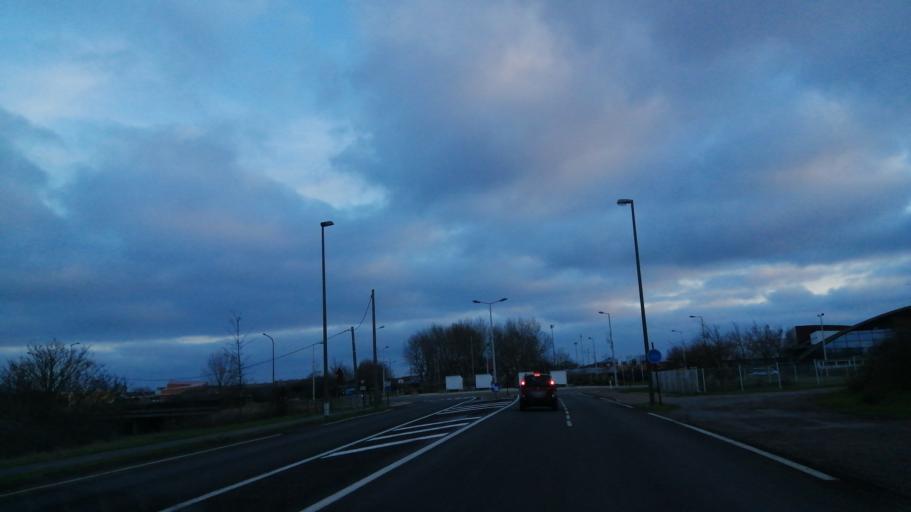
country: FR
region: Nord-Pas-de-Calais
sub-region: Departement du Pas-de-Calais
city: Calais
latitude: 50.9528
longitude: 1.8313
